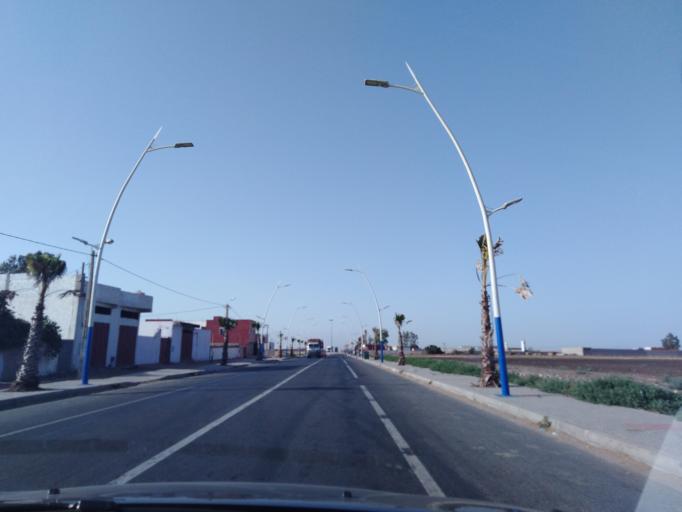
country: MA
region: Doukkala-Abda
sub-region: El-Jadida
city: Sidi Bennour
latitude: 32.5862
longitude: -8.7109
